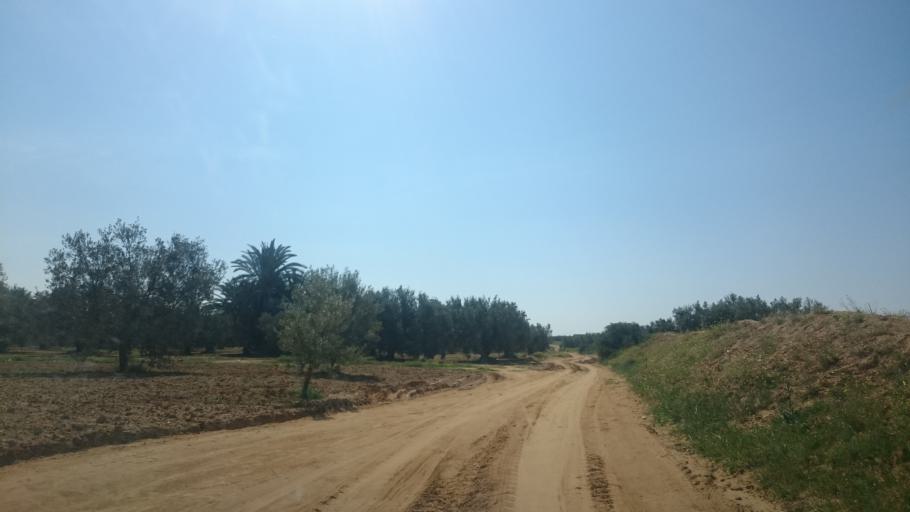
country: TN
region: Safaqis
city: Sfax
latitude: 34.7563
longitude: 10.5084
